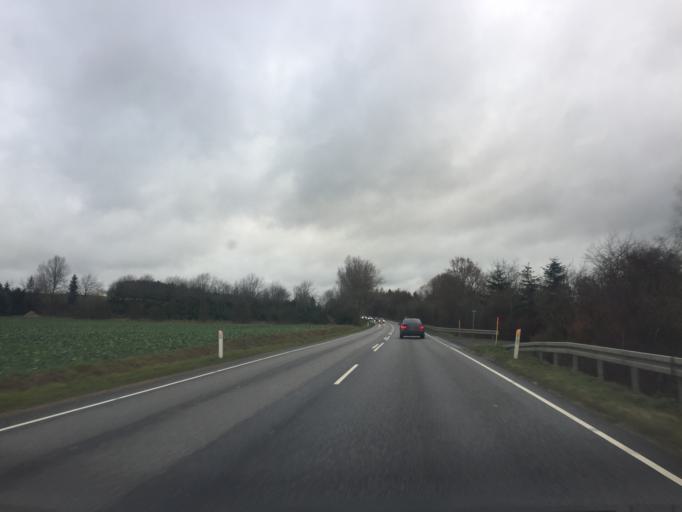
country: DK
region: Zealand
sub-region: Soro Kommune
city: Stenlille
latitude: 55.5123
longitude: 11.5818
